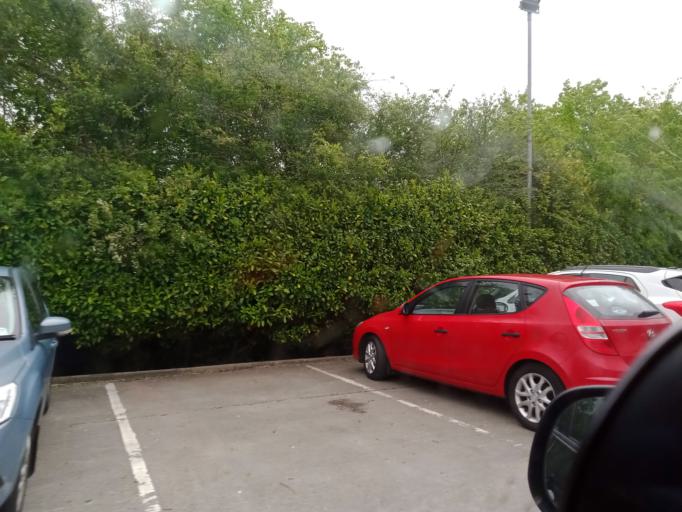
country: IE
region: Munster
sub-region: County Cork
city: Clonakilty
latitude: 51.6215
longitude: -8.9044
